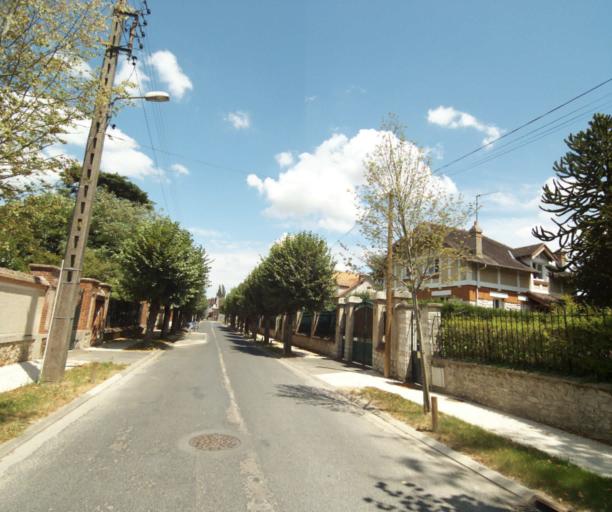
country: FR
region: Ile-de-France
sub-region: Departement de Seine-et-Marne
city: Hericy
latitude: 48.4425
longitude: 2.7579
